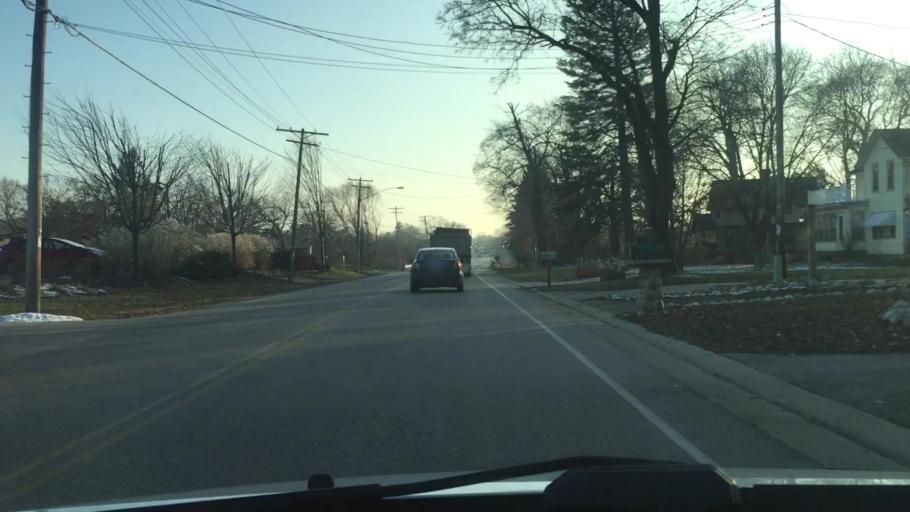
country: US
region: Wisconsin
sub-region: Waukesha County
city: Dousman
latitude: 43.0211
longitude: -88.4726
